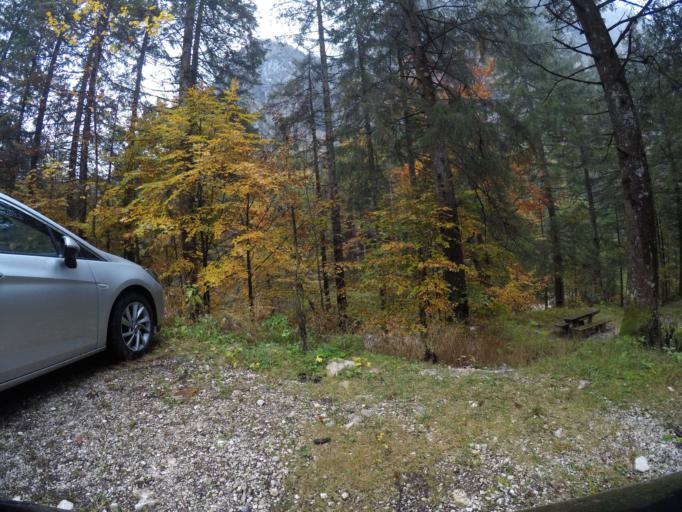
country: SI
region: Kranjska Gora
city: Kranjska Gora
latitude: 46.3839
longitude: 13.7733
